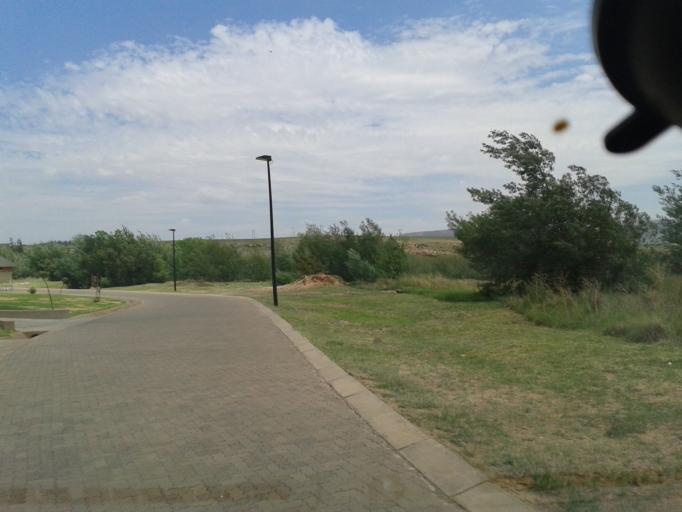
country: LS
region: Maseru
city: Maseru
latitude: -29.3448
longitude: 27.6621
